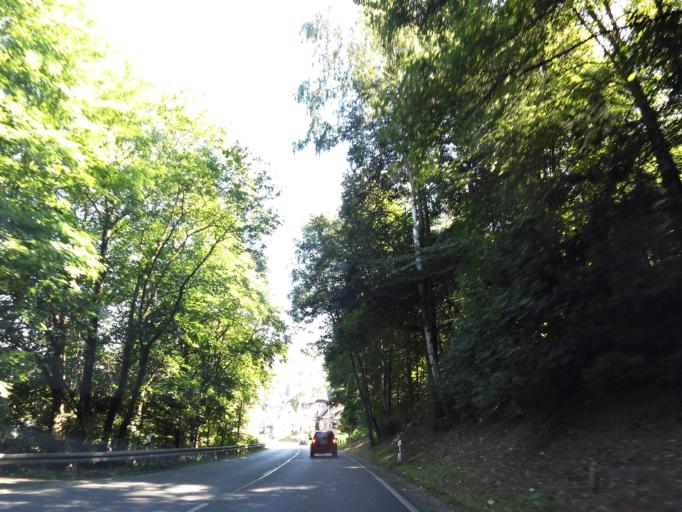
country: DE
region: Saxony
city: Konigstein
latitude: 50.9203
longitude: 14.0644
